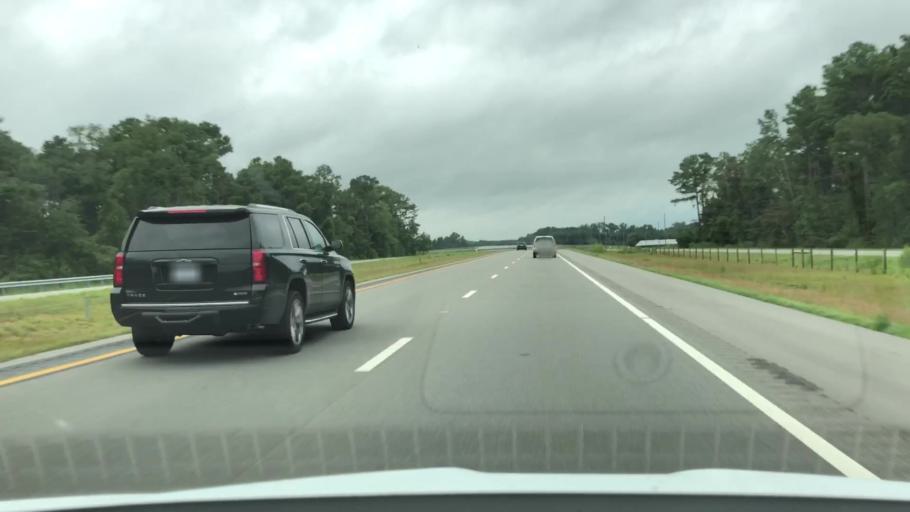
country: US
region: North Carolina
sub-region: Wayne County
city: Elroy
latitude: 35.3506
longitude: -77.8474
